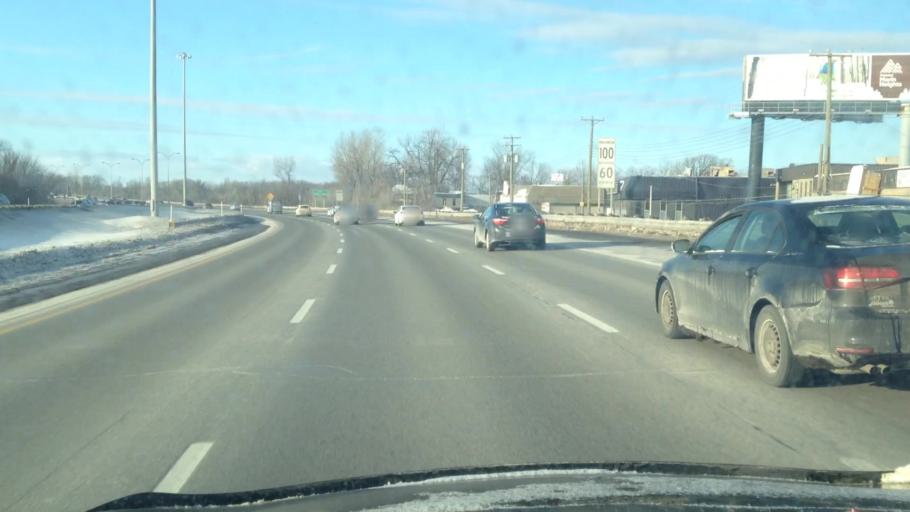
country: CA
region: Quebec
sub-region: Laurentides
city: Boisbriand
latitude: 45.6044
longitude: -73.8056
